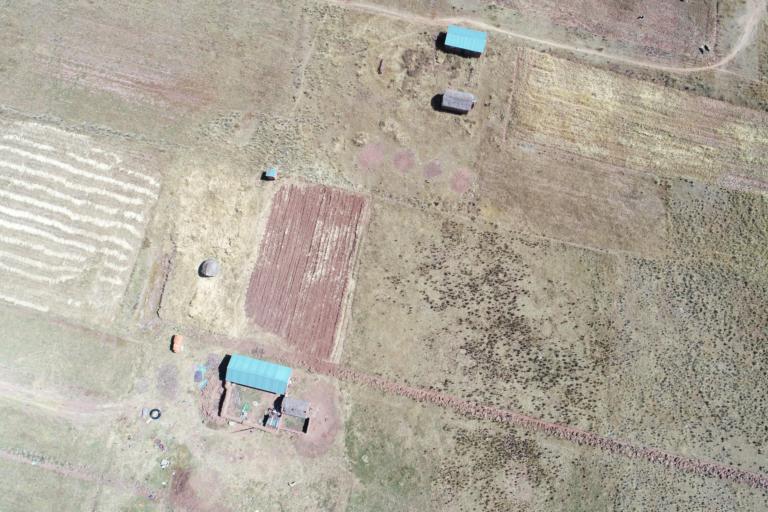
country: BO
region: La Paz
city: Tiahuanaco
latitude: -16.5931
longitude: -68.7746
